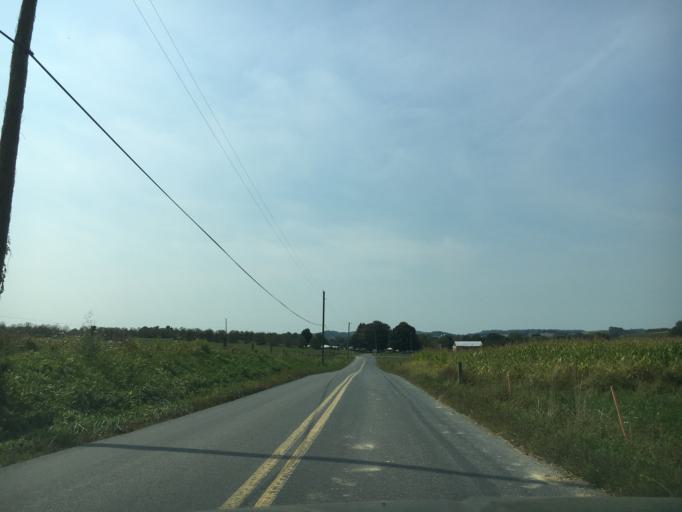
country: US
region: Pennsylvania
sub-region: Berks County
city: Topton
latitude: 40.5513
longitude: -75.7132
